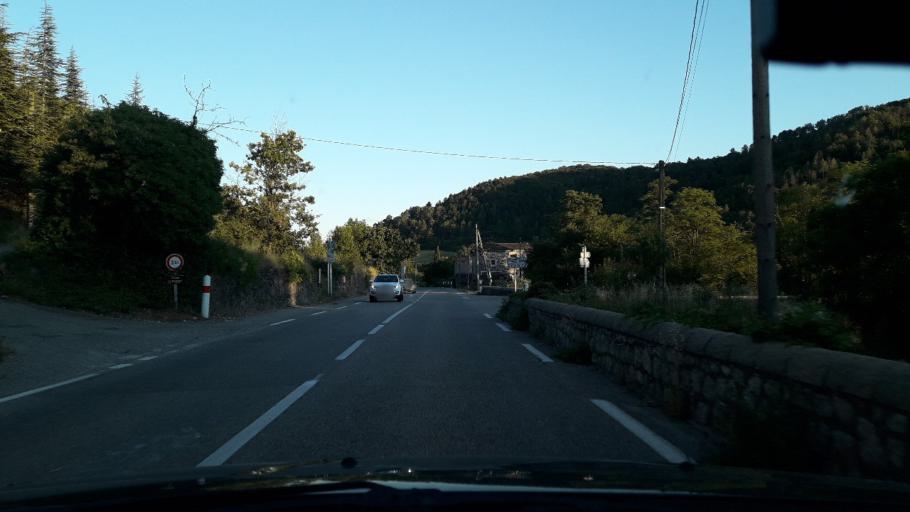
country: FR
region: Rhone-Alpes
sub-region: Departement de l'Ardeche
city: Alba-la-Romaine
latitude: 44.5524
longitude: 4.6062
